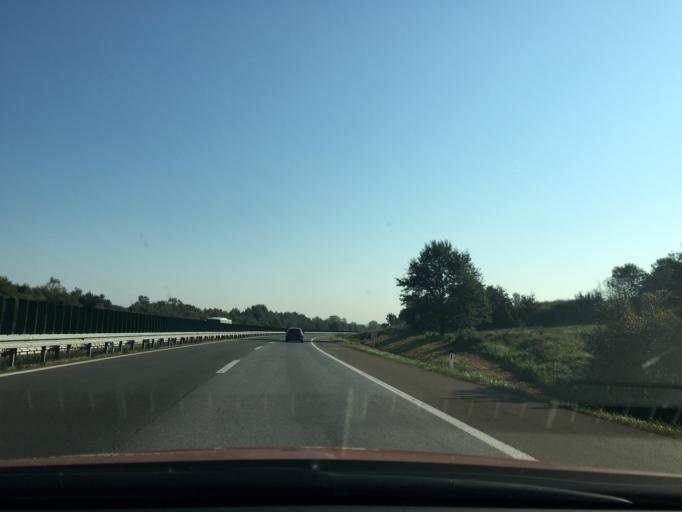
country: RS
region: Central Serbia
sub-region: Belgrade
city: Grocka
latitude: 44.5741
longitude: 20.7261
